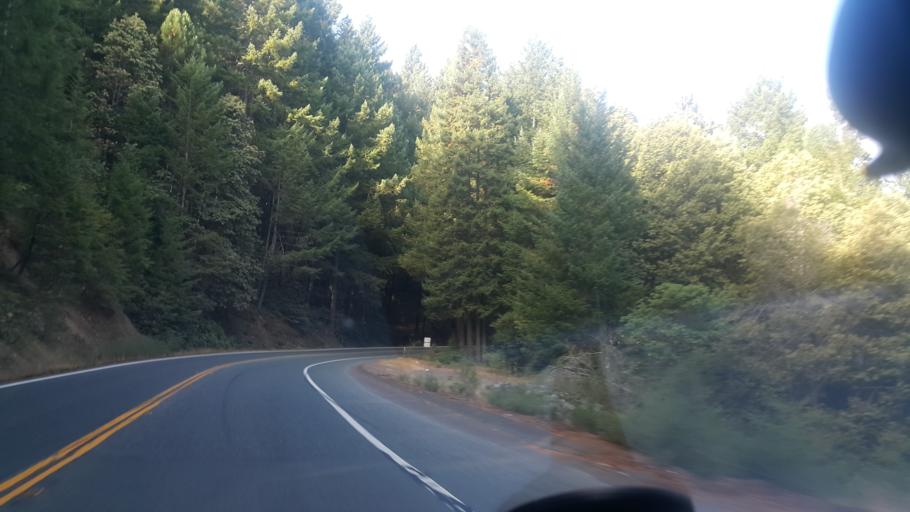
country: US
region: California
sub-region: Mendocino County
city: Brooktrails
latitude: 39.3930
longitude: -123.4608
